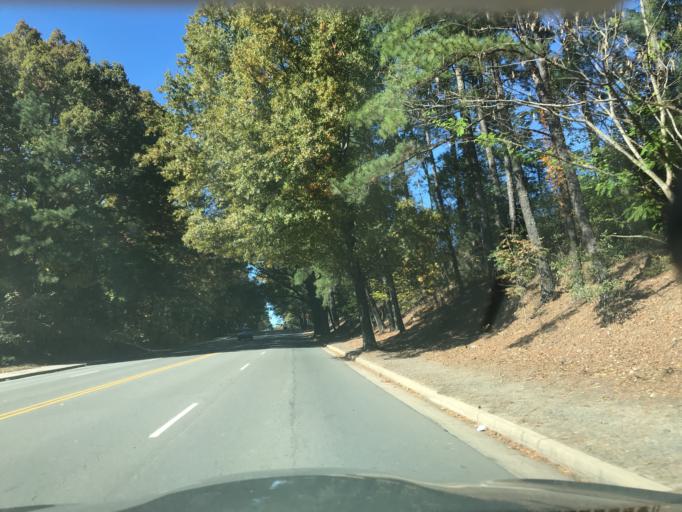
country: US
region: North Carolina
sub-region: Durham County
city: Durham
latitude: 35.9936
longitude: -78.9449
